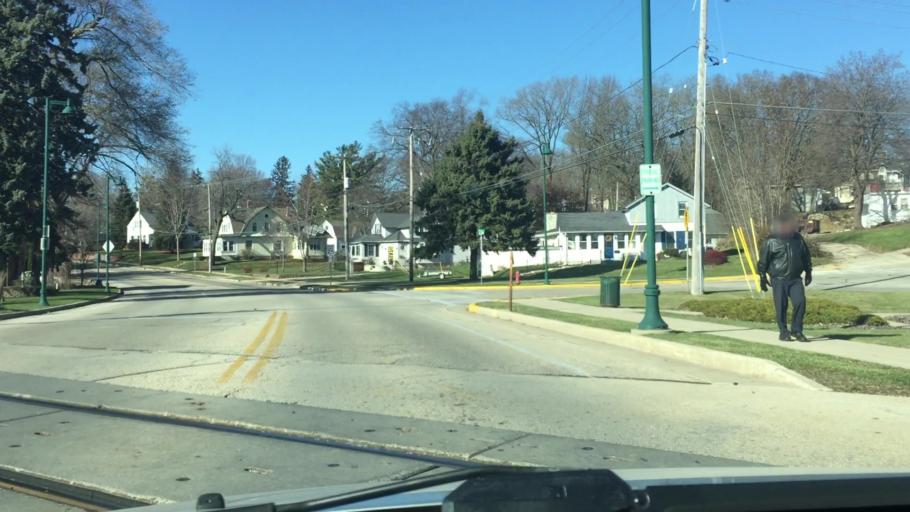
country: US
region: Wisconsin
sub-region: Waukesha County
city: Pewaukee
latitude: 43.0853
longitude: -88.2655
